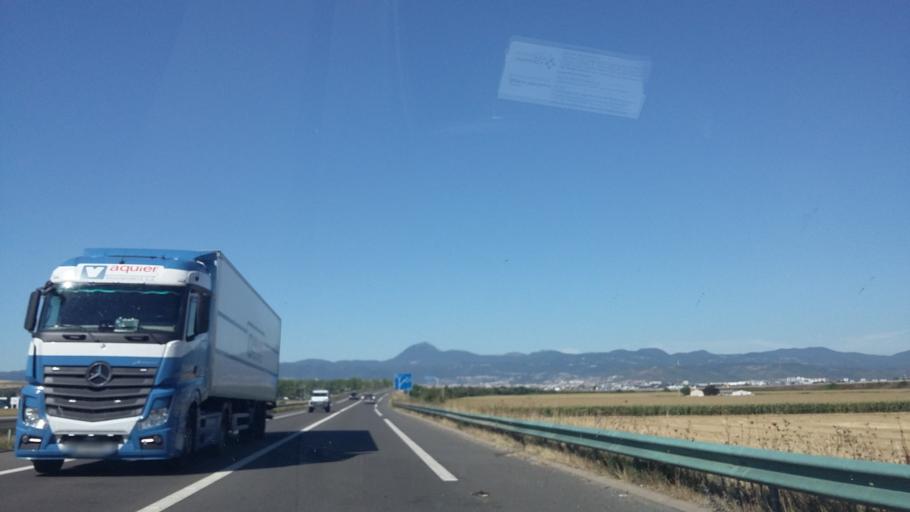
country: FR
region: Auvergne
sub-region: Departement du Puy-de-Dome
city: Dallet
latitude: 45.7851
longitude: 3.2095
